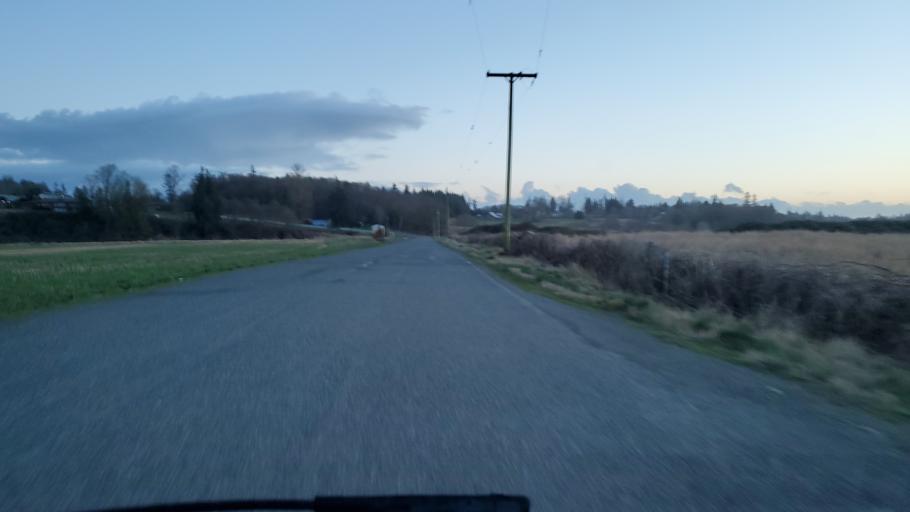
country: US
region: Washington
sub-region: Skagit County
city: Burlington
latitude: 48.4640
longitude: -122.2974
